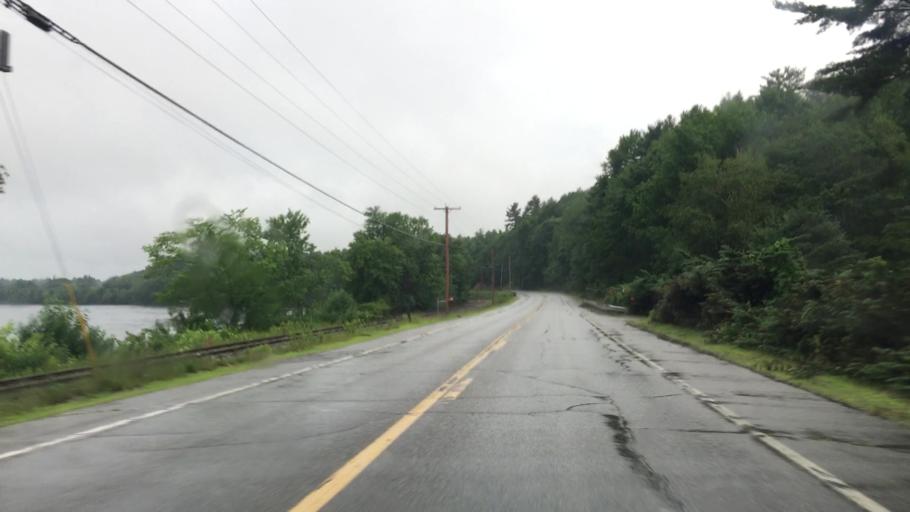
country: US
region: Maine
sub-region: Kennebec County
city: Pittston
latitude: 44.2084
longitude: -69.7643
